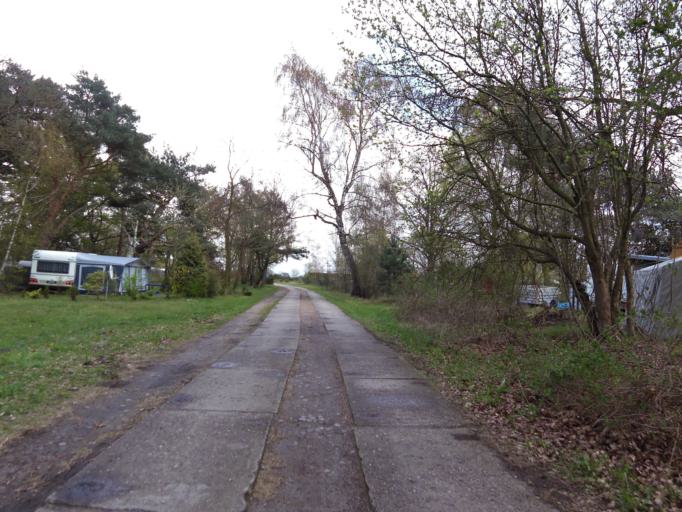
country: DE
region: Mecklenburg-Vorpommern
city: Born
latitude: 54.3825
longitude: 12.5026
